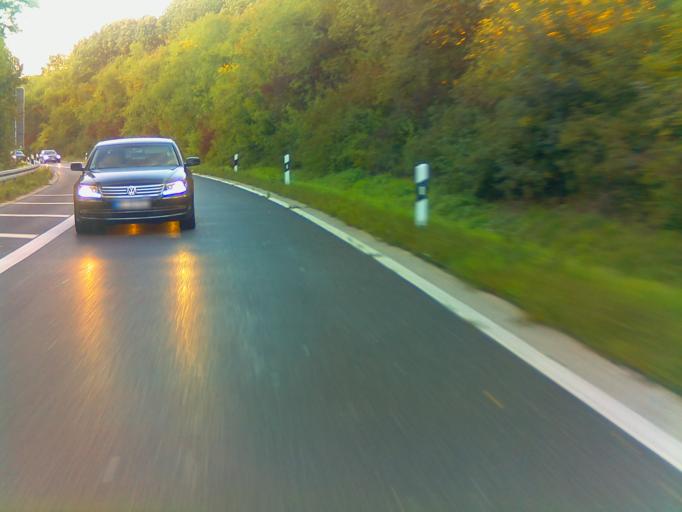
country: DE
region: Hesse
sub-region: Regierungsbezirk Darmstadt
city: Bad Homburg vor der Hoehe
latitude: 50.2077
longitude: 8.6249
